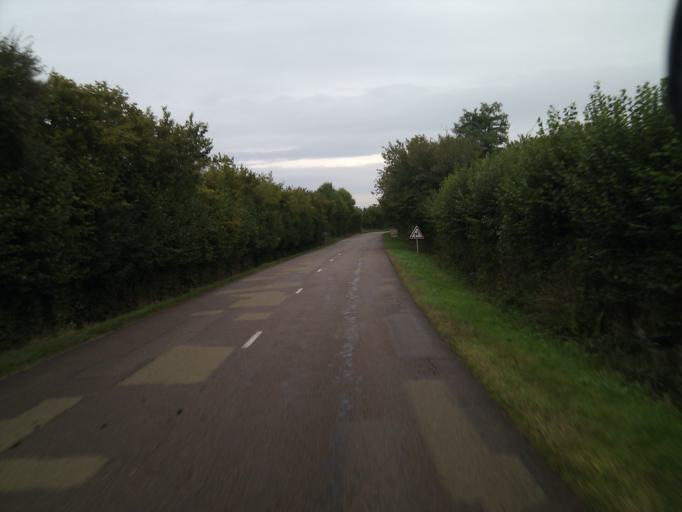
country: FR
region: Bourgogne
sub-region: Departement de la Cote-d'Or
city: Saulieu
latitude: 47.2752
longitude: 4.2191
